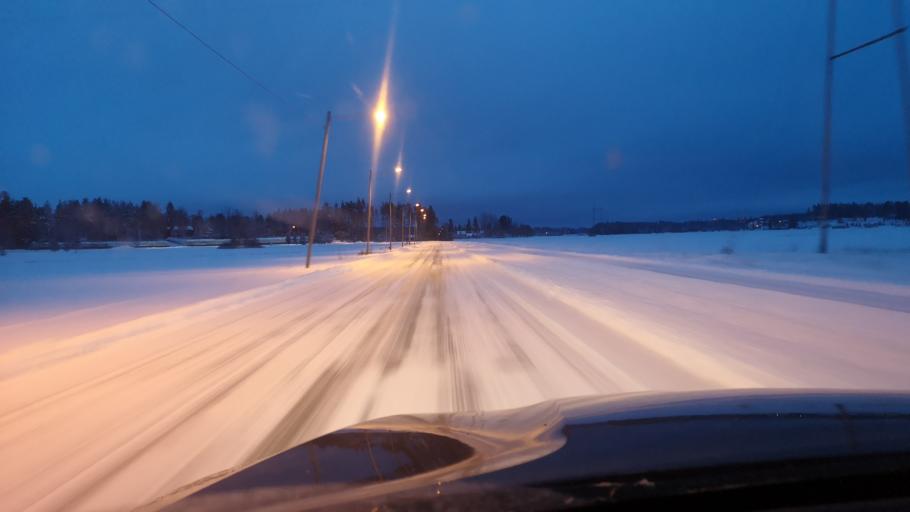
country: FI
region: Varsinais-Suomi
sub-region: Loimaa
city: Loimaa
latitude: 60.8611
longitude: 23.0753
